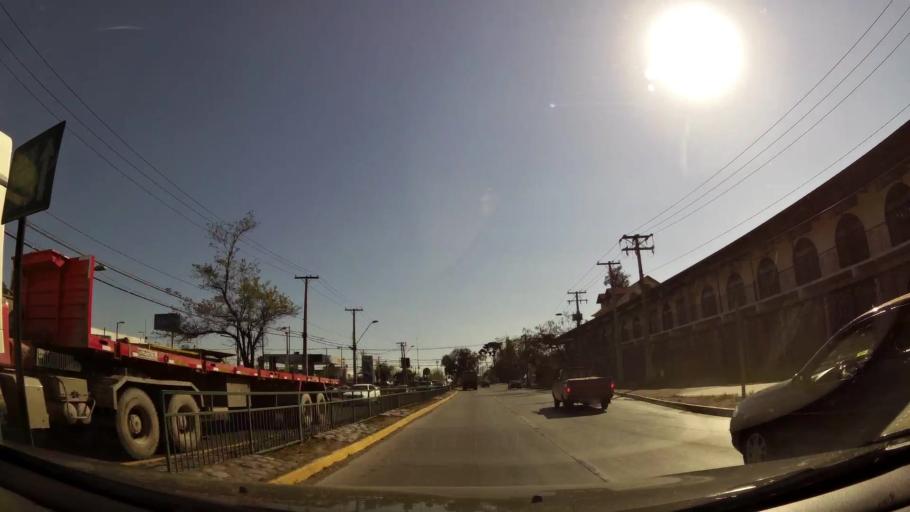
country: CL
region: Santiago Metropolitan
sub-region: Provincia de Santiago
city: La Pintana
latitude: -33.5855
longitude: -70.6276
